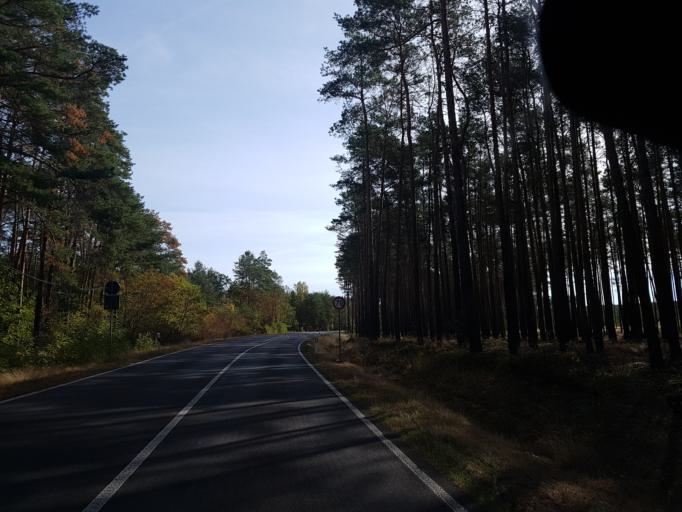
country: DE
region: Brandenburg
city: Schlieben
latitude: 51.6899
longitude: 13.4431
